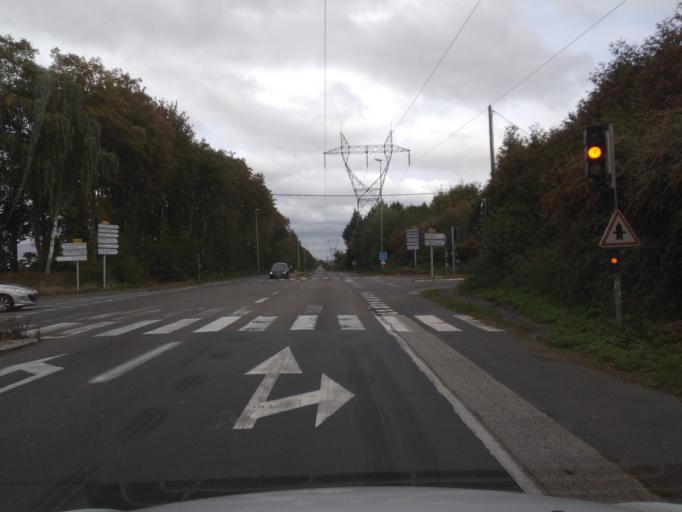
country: FR
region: Nord-Pas-de-Calais
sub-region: Departement du Nord
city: Saint-Saulve
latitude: 50.3611
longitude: 3.5637
